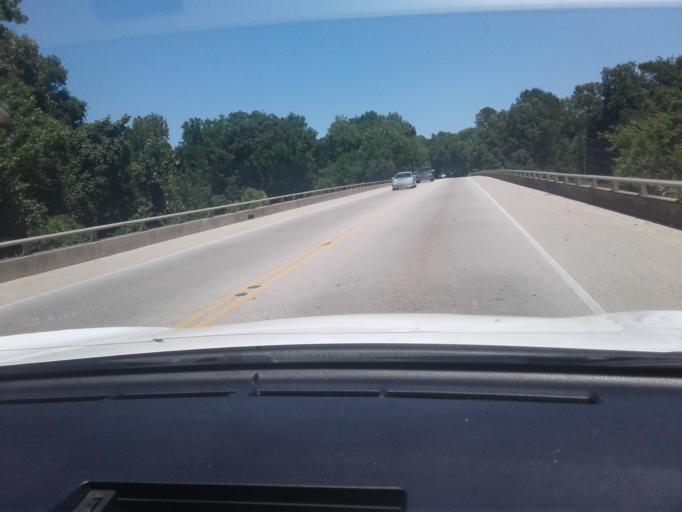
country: US
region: North Carolina
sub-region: Harnett County
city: Erwin
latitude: 35.3120
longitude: -78.6937
